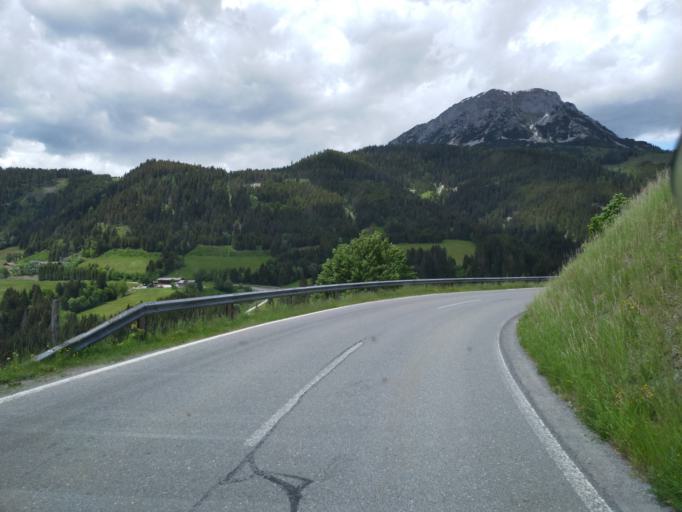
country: AT
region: Salzburg
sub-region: Politischer Bezirk Sankt Johann im Pongau
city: Filzmoos
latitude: 47.4323
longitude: 13.5801
